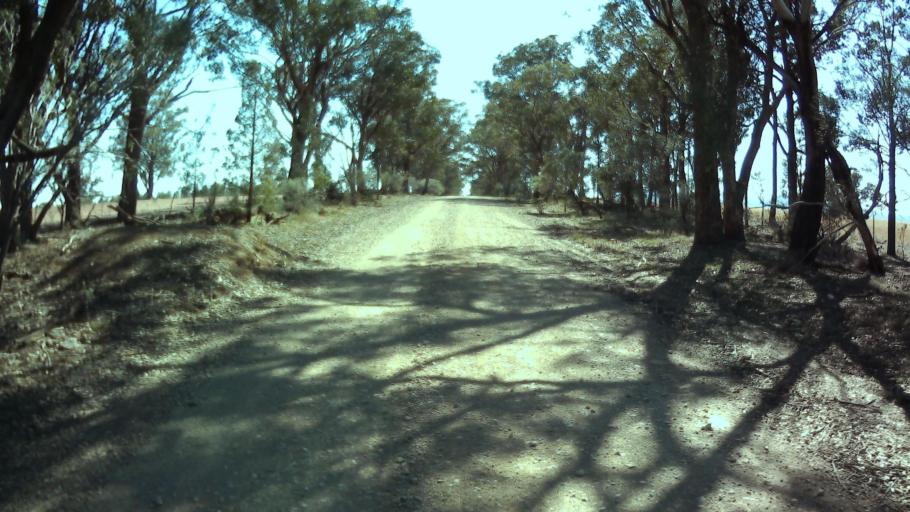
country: AU
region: New South Wales
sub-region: Weddin
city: Grenfell
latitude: -33.9059
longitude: 147.8550
